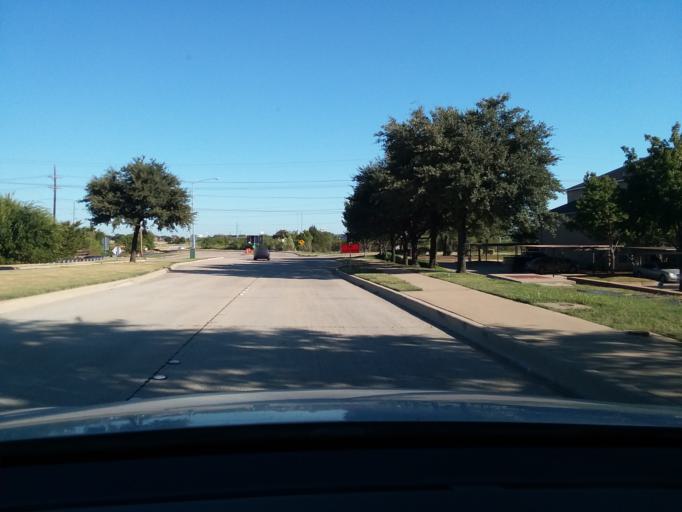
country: US
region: Texas
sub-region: Denton County
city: Lewisville
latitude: 33.0633
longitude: -97.0200
